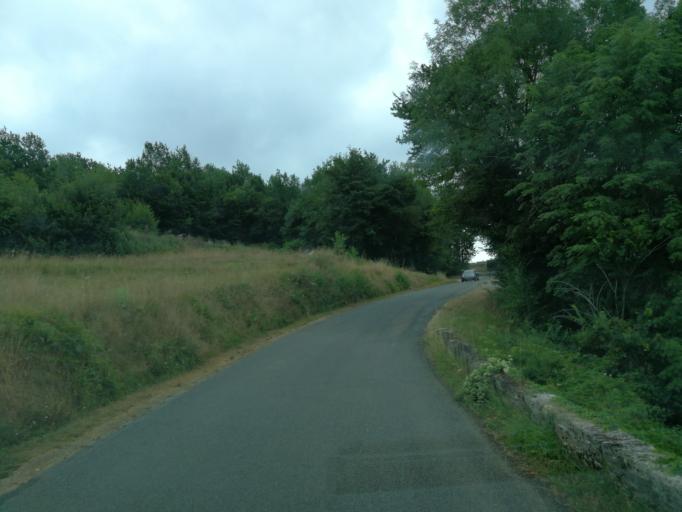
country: FR
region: Aquitaine
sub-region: Departement du Lot-et-Garonne
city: Montayral
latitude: 44.5412
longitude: 1.0764
